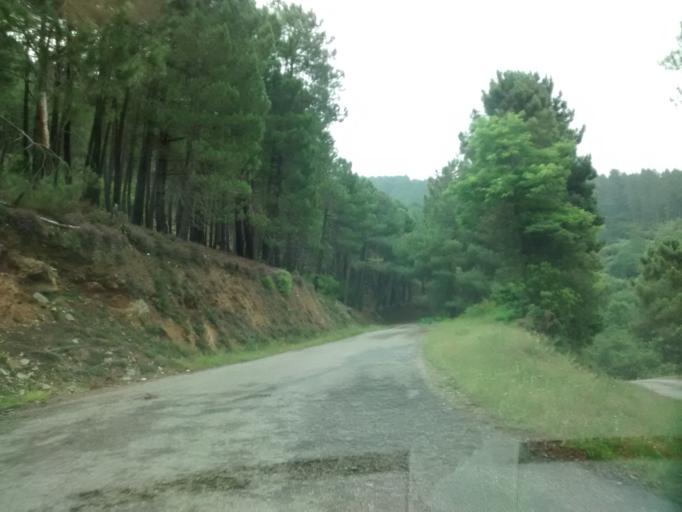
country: ES
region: Galicia
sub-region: Provincia de Ourense
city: Castro Caldelas
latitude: 42.4171
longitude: -7.3882
